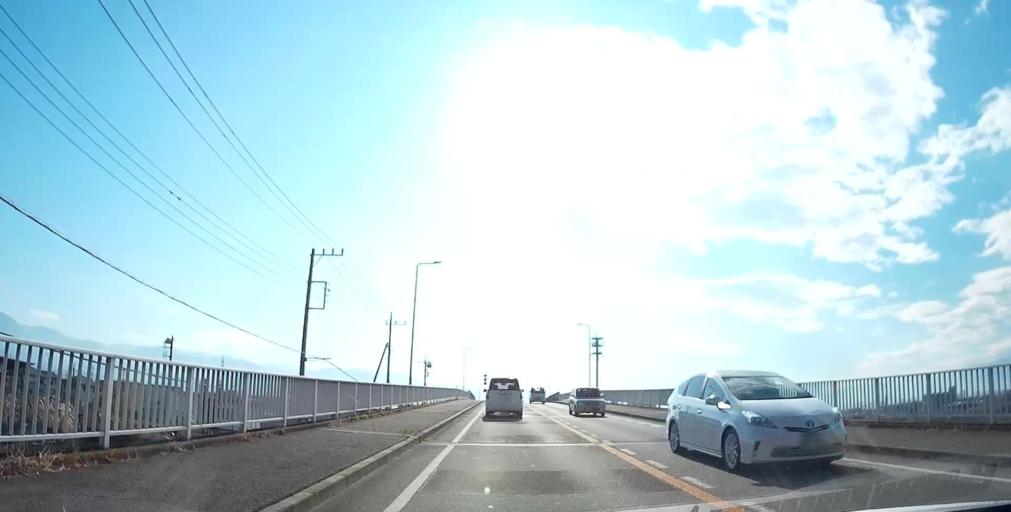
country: JP
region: Yamanashi
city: Isawa
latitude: 35.6574
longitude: 138.6147
